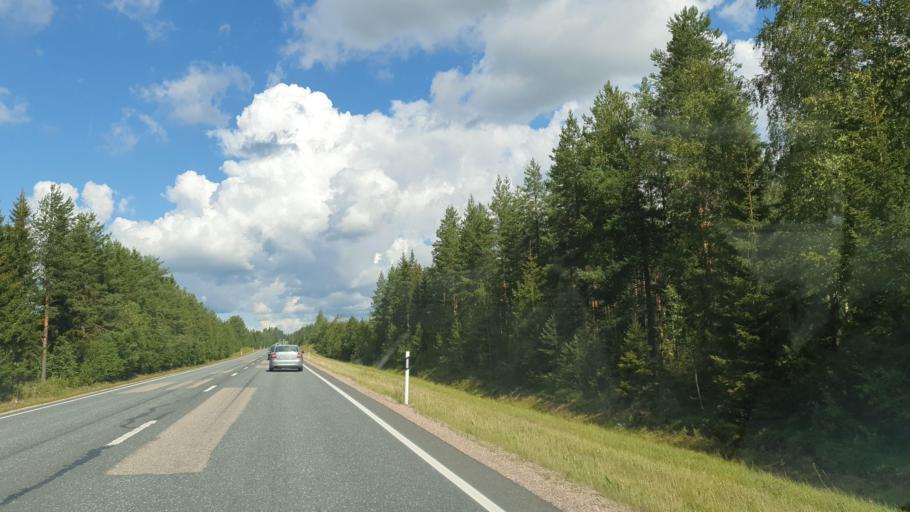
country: FI
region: Kainuu
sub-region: Kajaani
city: Kajaani
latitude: 64.0416
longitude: 27.4495
